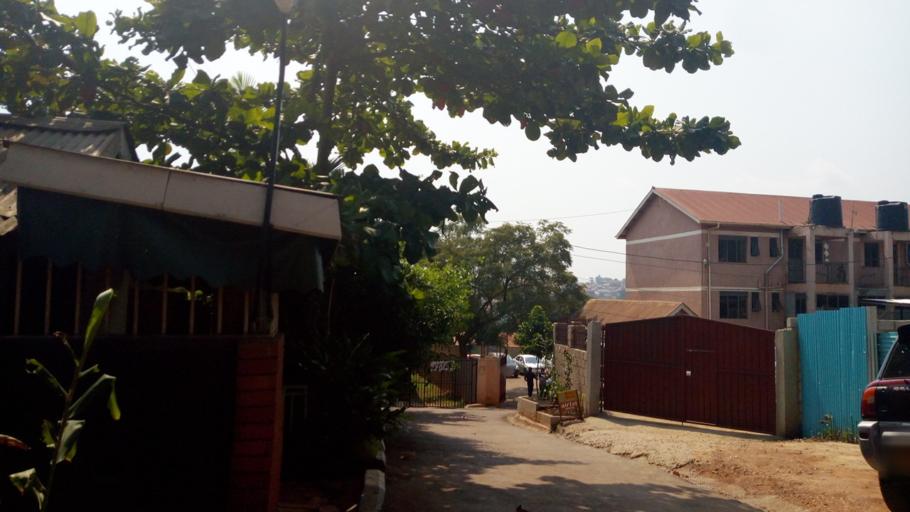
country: UG
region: Central Region
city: Kampala Central Division
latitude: 0.3429
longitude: 32.5676
